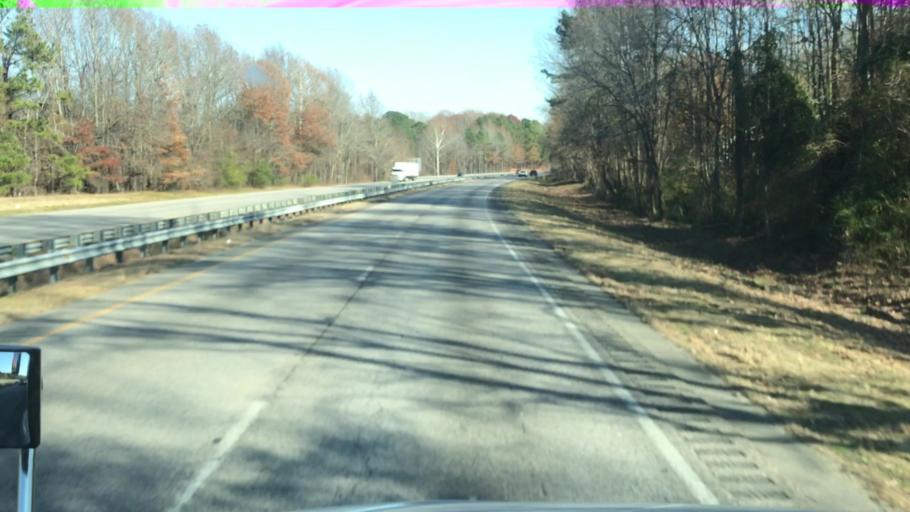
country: US
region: North Carolina
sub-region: Nash County
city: Nashville
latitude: 35.9761
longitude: -77.9295
